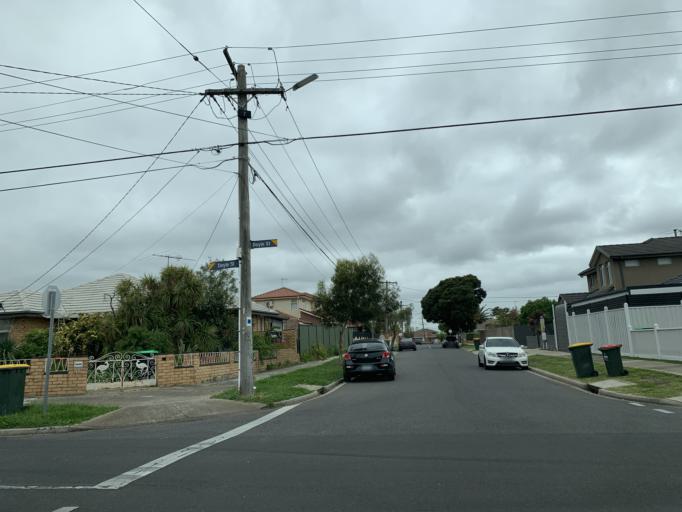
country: AU
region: Victoria
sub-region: Moonee Valley
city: Essendon West
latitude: -37.7576
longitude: 144.8577
